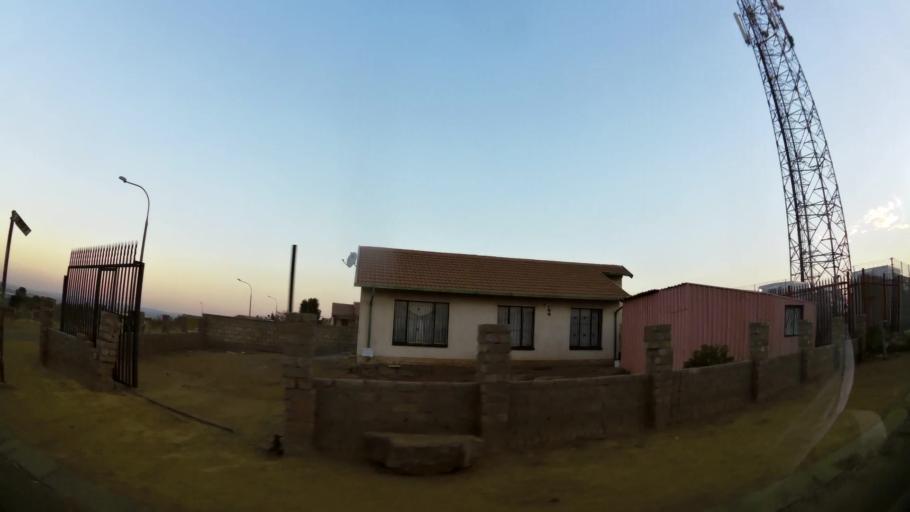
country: ZA
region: Gauteng
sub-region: West Rand District Municipality
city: Randfontein
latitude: -26.2049
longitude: 27.7190
